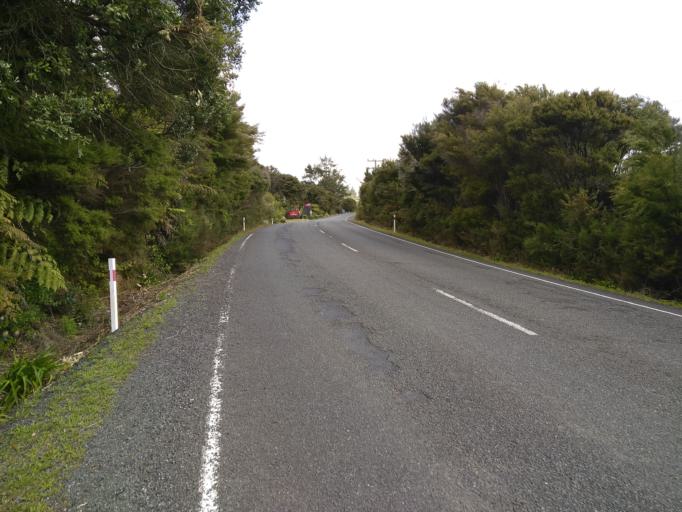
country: NZ
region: Northland
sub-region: Far North District
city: Paihia
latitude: -35.2827
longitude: 174.1475
